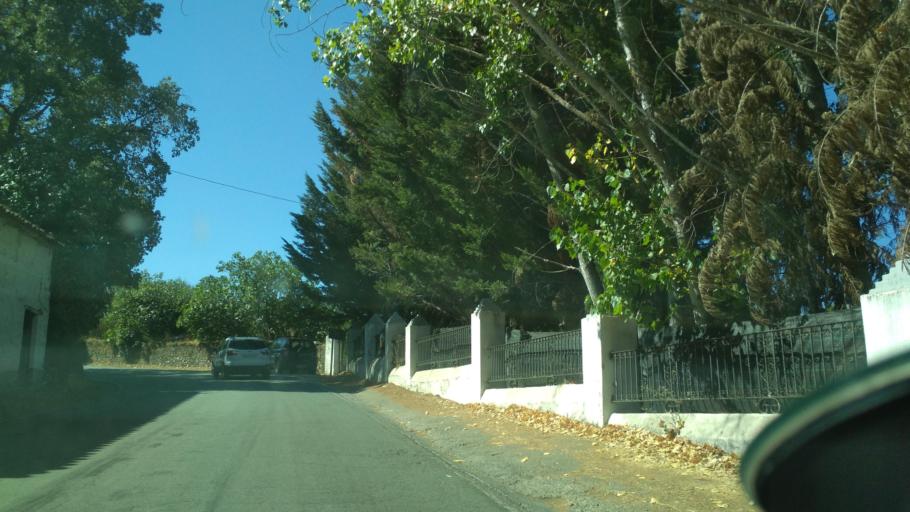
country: ES
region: Andalusia
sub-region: Provincia de Huelva
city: Galaroza
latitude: 37.9233
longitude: -6.7068
